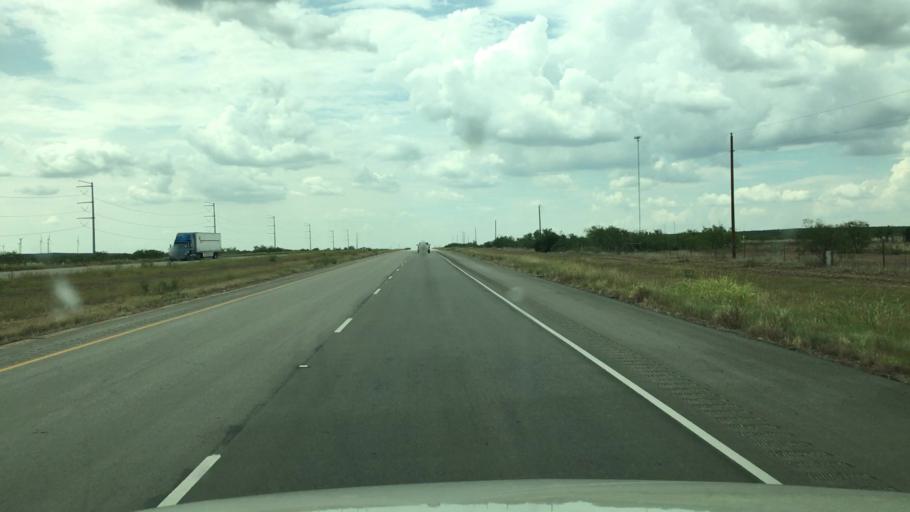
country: US
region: Texas
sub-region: Glasscock County
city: Garden City
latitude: 31.9760
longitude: -101.2486
